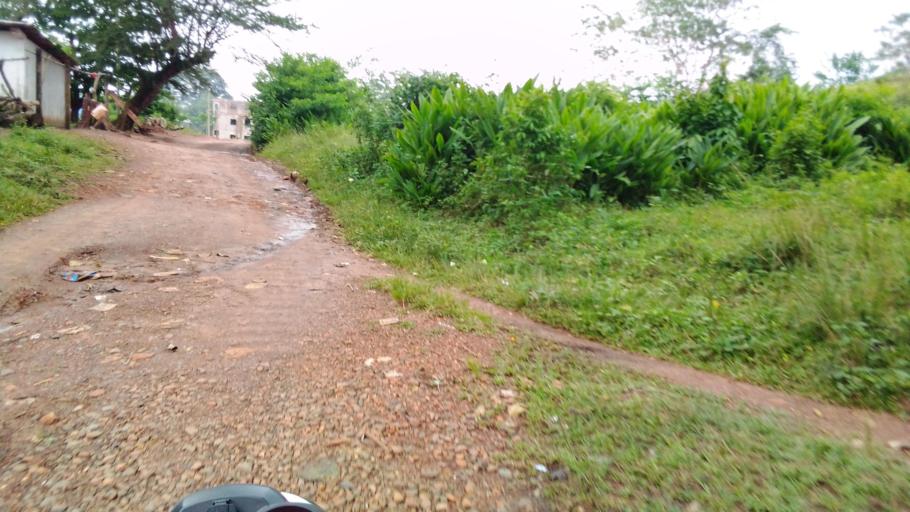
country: SL
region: Eastern Province
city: Kenema
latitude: 7.8876
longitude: -11.1961
